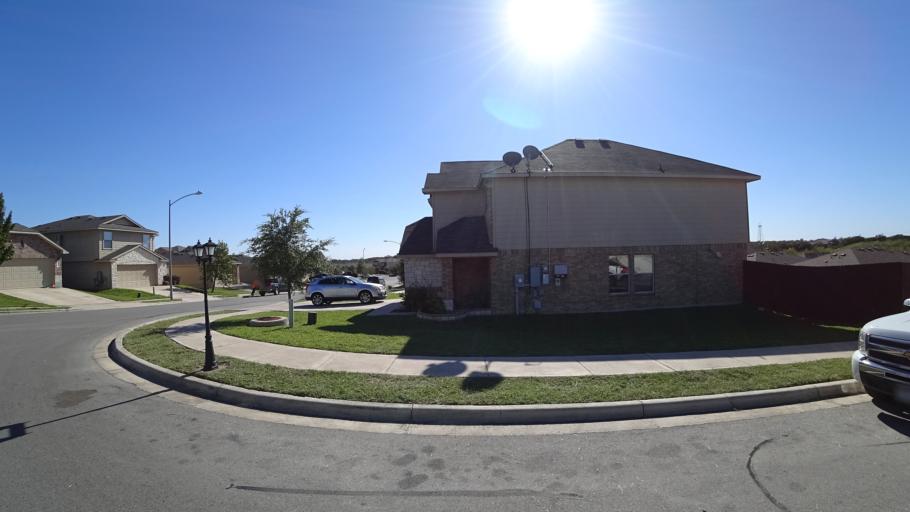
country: US
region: Texas
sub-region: Travis County
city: Hornsby Bend
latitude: 30.2819
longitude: -97.6289
